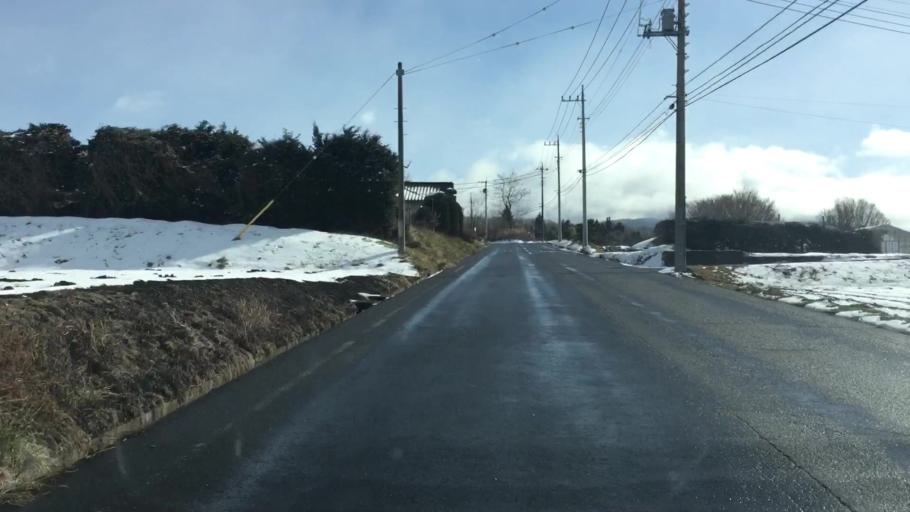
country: JP
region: Gunma
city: Numata
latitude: 36.6064
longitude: 139.0928
